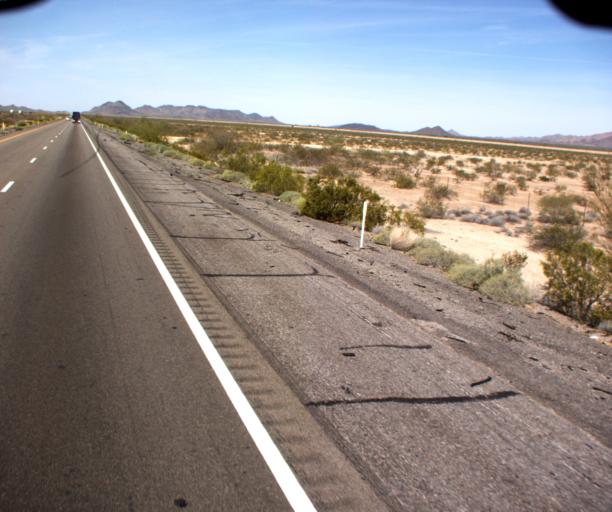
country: US
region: Arizona
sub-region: La Paz County
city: Salome
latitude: 33.5978
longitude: -113.5424
